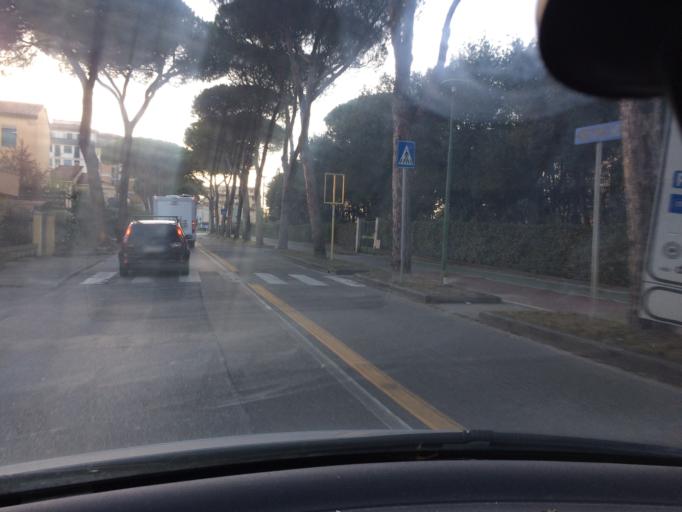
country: IT
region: Tuscany
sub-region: Province of Pisa
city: Pisa
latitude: 43.7220
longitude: 10.4171
